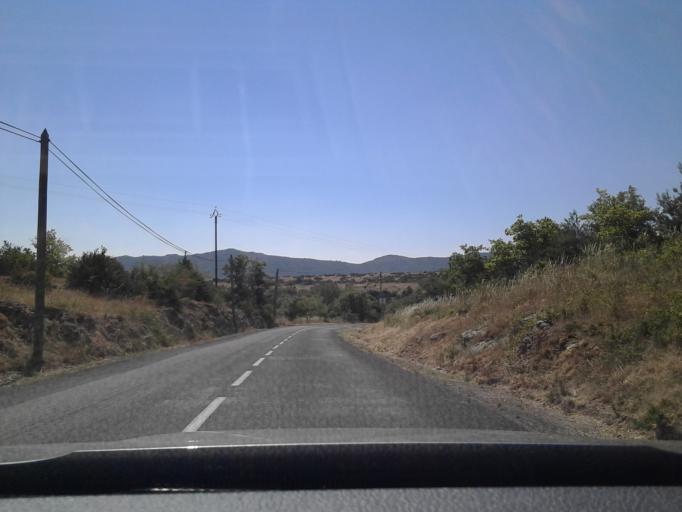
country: FR
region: Languedoc-Roussillon
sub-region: Departement de l'Herault
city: Montpeyroux
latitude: 43.7790
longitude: 3.4660
